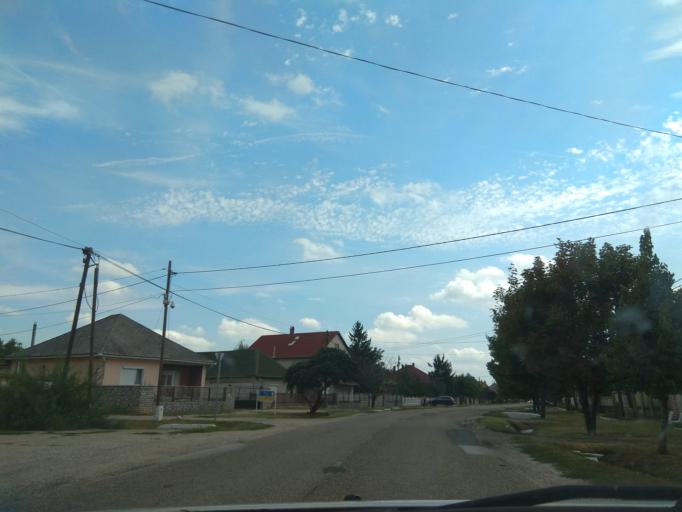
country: HU
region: Borsod-Abauj-Zemplen
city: Sajolad
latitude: 48.0390
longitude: 20.8860
